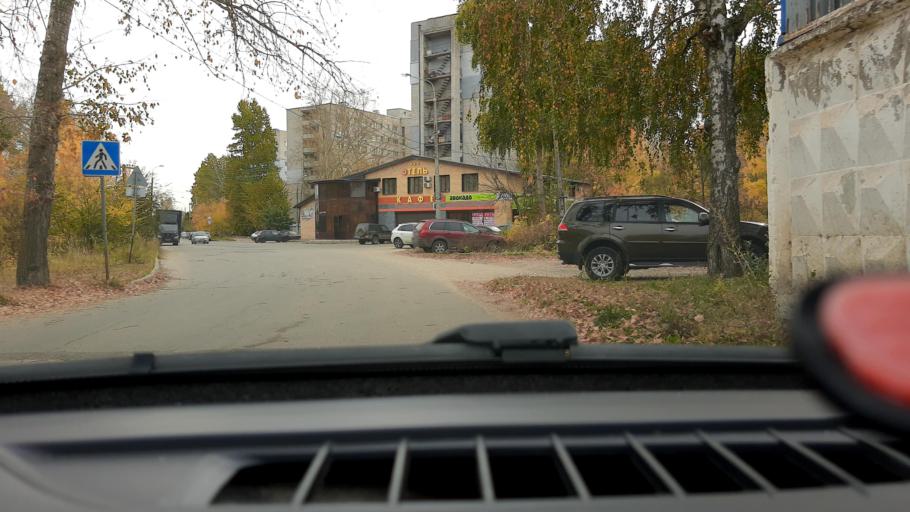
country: RU
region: Nizjnij Novgorod
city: Gorbatovka
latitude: 56.2922
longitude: 43.8396
